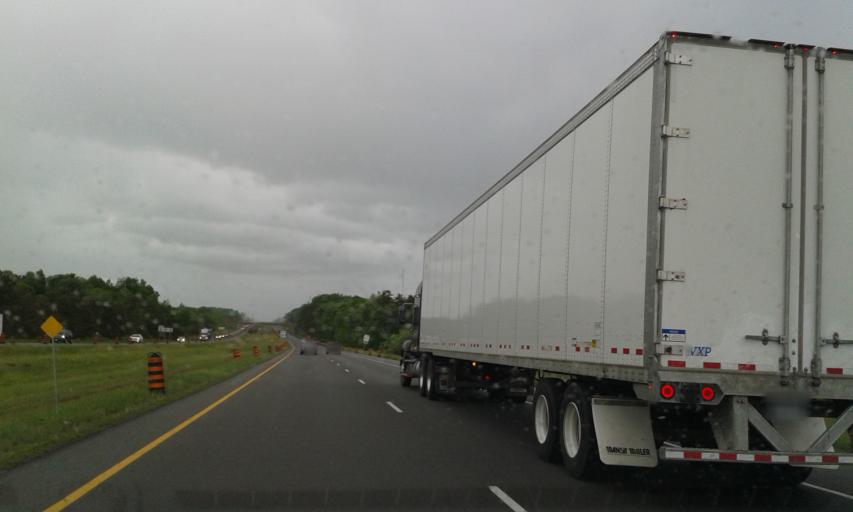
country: CA
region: Ontario
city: Gananoque
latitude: 44.3511
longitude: -76.1050
